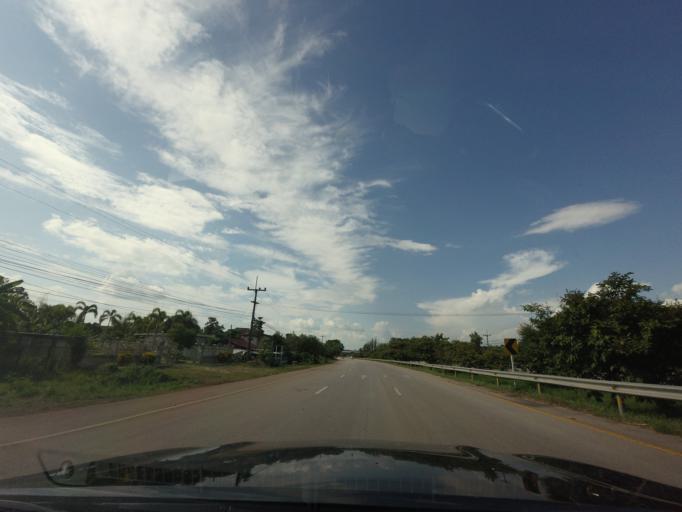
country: TH
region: Nong Khai
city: Sa Khrai
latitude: 17.6731
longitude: 102.7900
